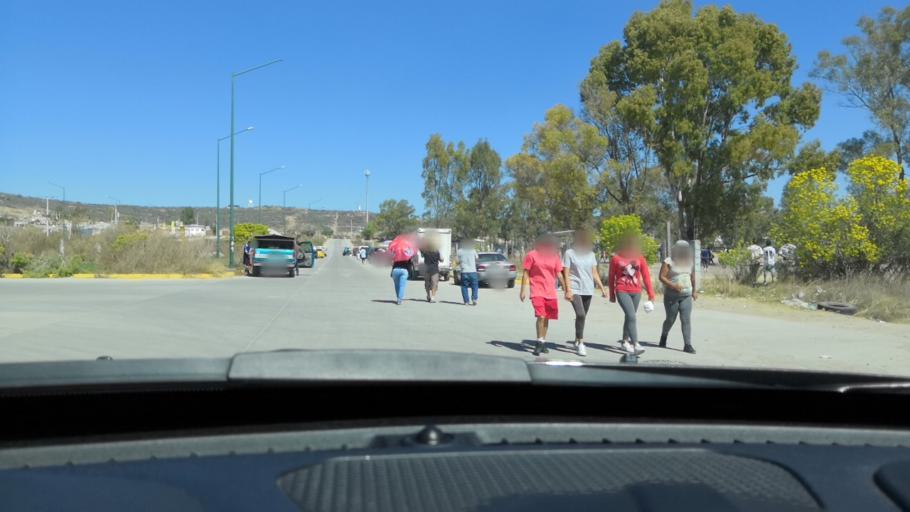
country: MX
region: Guanajuato
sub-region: Leon
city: Rizos de la Joya (Rizos del Saucillo)
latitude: 21.1478
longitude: -101.7548
